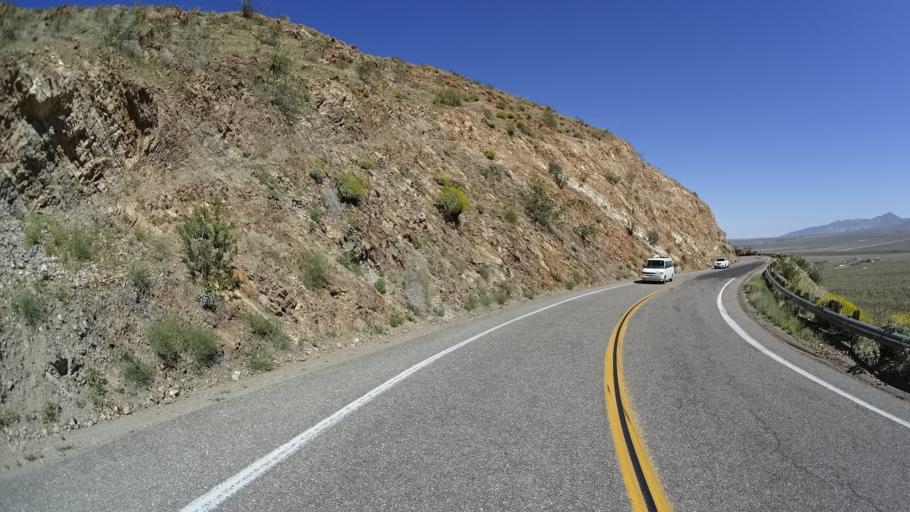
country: US
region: California
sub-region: San Diego County
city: Borrego Springs
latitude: 33.2374
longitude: -116.4078
